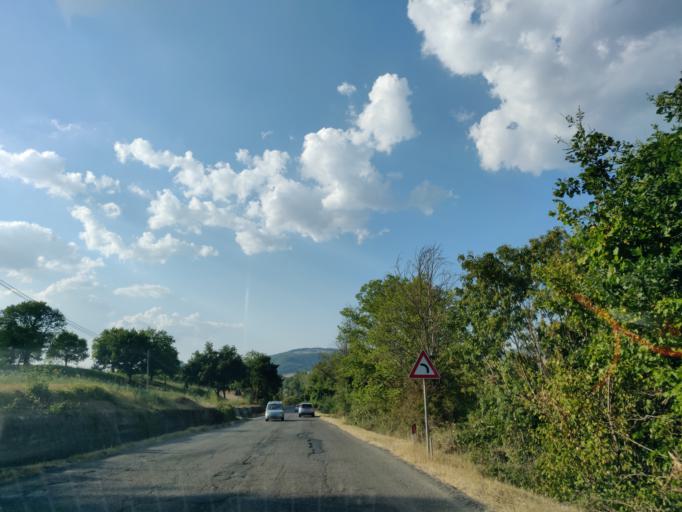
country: IT
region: Latium
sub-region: Provincia di Viterbo
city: Acquapendente
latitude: 42.7591
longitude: 11.8642
